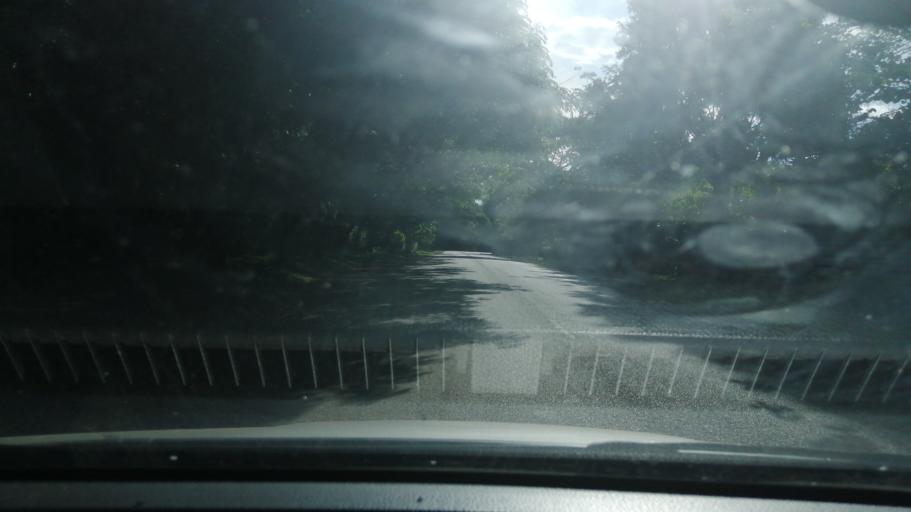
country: ZW
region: Harare
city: Harare
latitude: -17.7652
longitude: 31.0593
